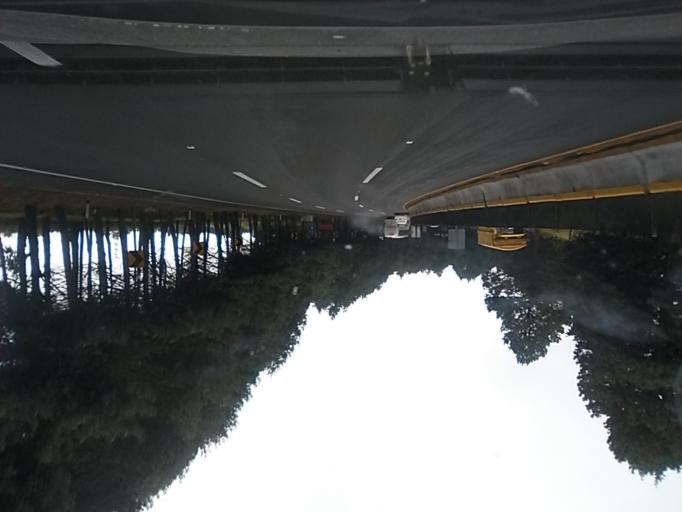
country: MX
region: Mexico City
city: Xochimilco
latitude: 19.1654
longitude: -99.1529
